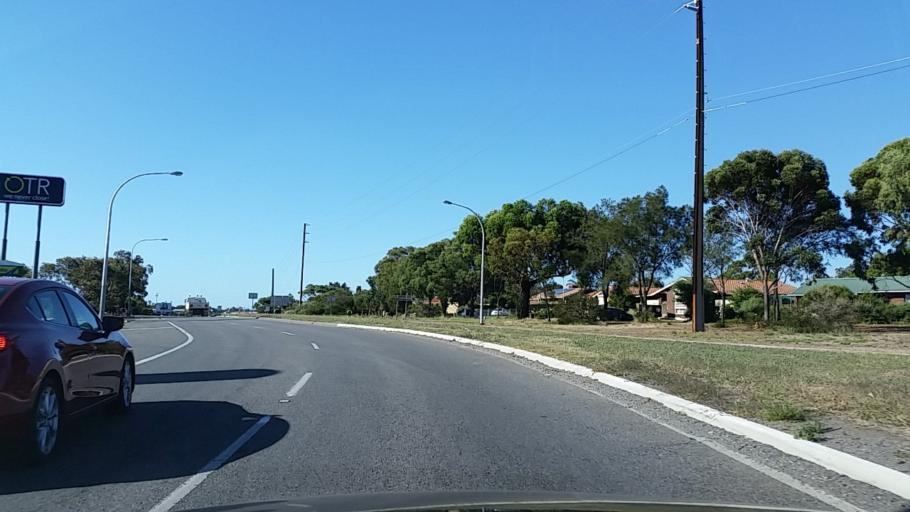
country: AU
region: South Australia
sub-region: Adelaide
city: Port Noarlunga
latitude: -35.1302
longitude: 138.4855
